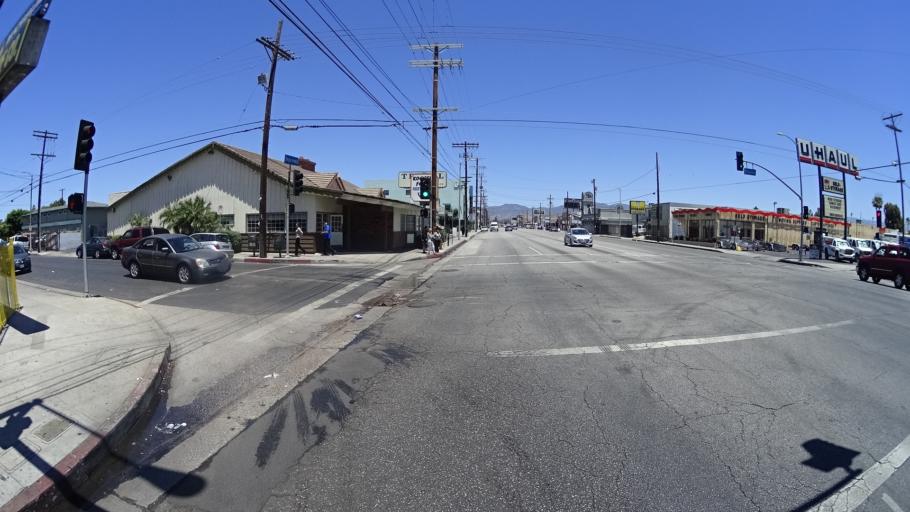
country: US
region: California
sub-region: Los Angeles County
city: Van Nuys
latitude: 34.2245
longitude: -118.4680
